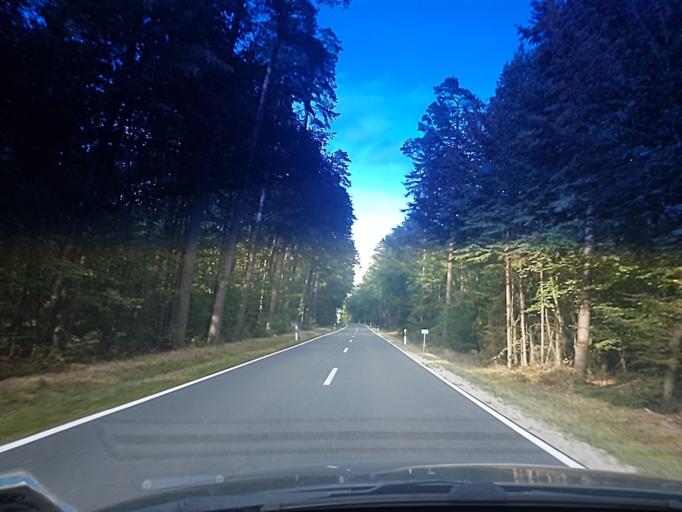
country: DE
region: Bavaria
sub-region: Upper Franconia
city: Burgwindheim
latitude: 49.7928
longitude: 10.5715
